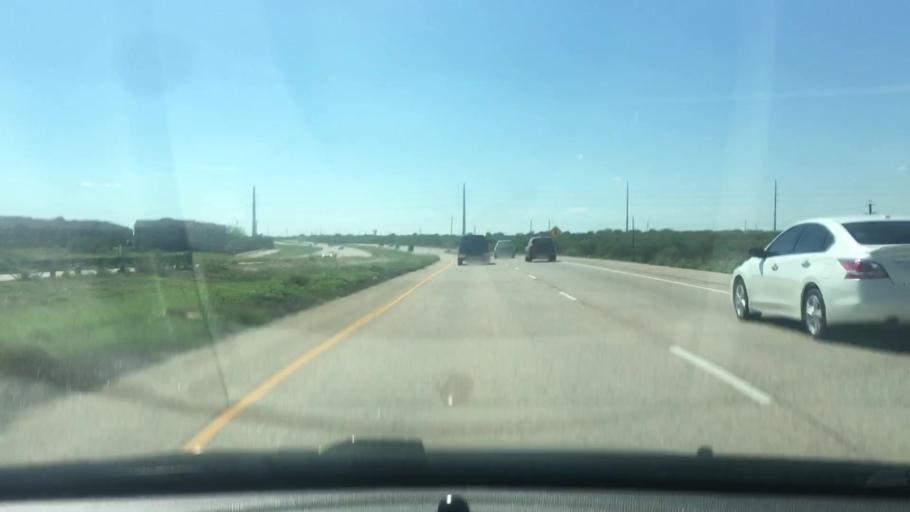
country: US
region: Texas
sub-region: Denton County
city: Denton
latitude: 33.2605
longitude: -97.1323
